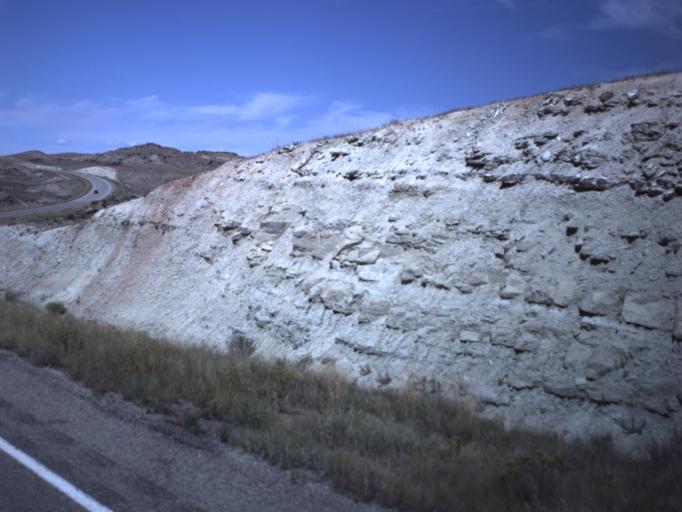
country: US
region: Colorado
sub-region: Montezuma County
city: Towaoc
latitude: 37.1720
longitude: -109.0959
